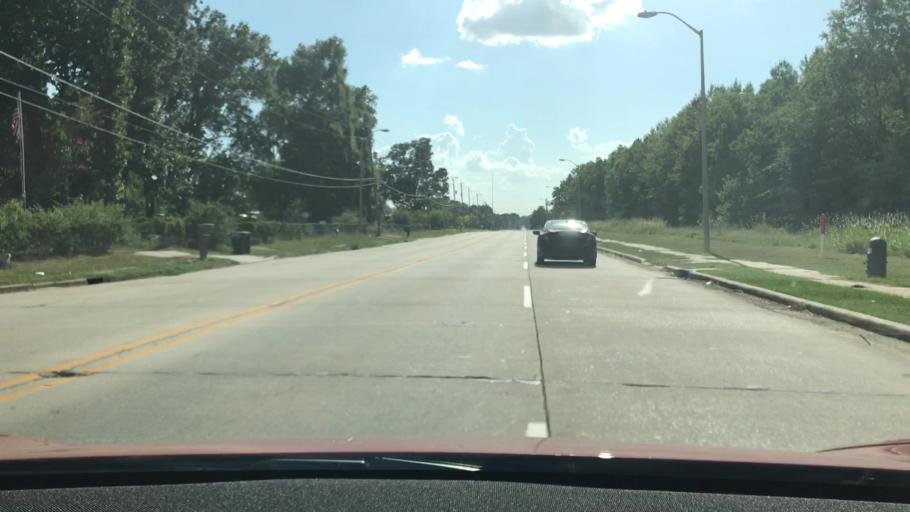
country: US
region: Louisiana
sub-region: Bossier Parish
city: Bossier City
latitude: 32.4130
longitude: -93.7649
